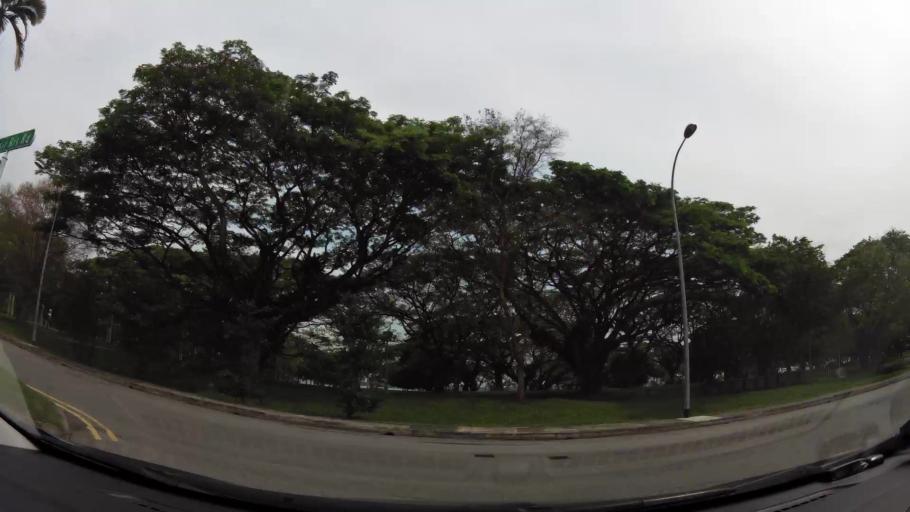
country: MY
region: Johor
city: Kampung Pasir Gudang Baru
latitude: 1.3824
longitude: 103.9460
